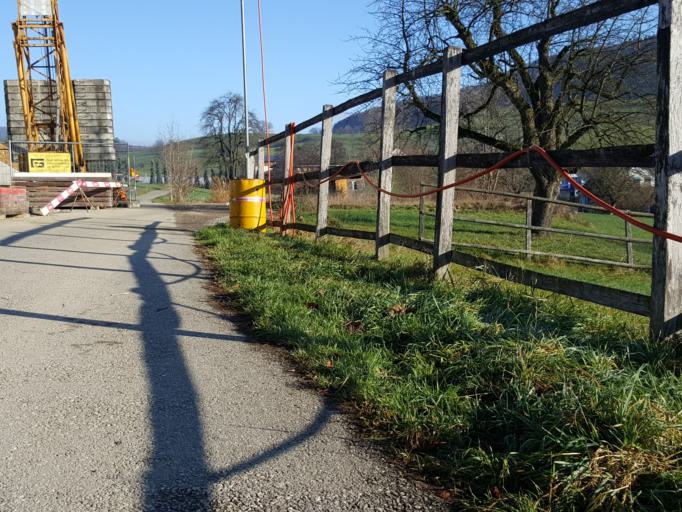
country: CH
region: Basel-Landschaft
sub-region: Bezirk Sissach
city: Ormalingen
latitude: 47.4739
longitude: 7.8749
